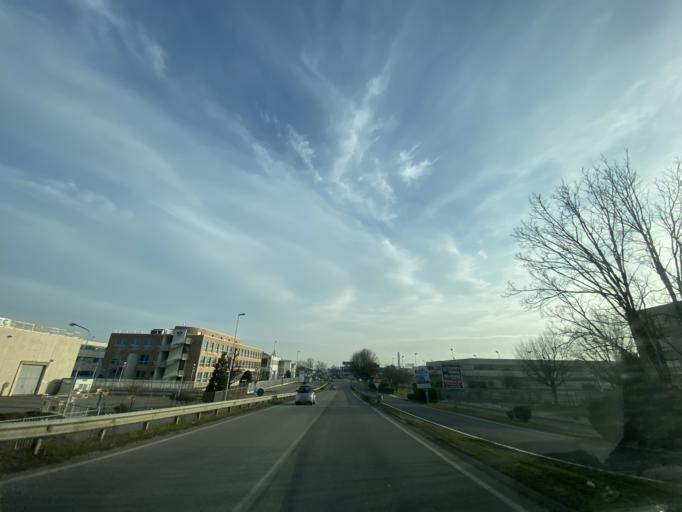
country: IT
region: Lombardy
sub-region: Citta metropolitana di Milano
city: Cassina de' Pecchi
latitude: 45.5188
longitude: 9.3485
